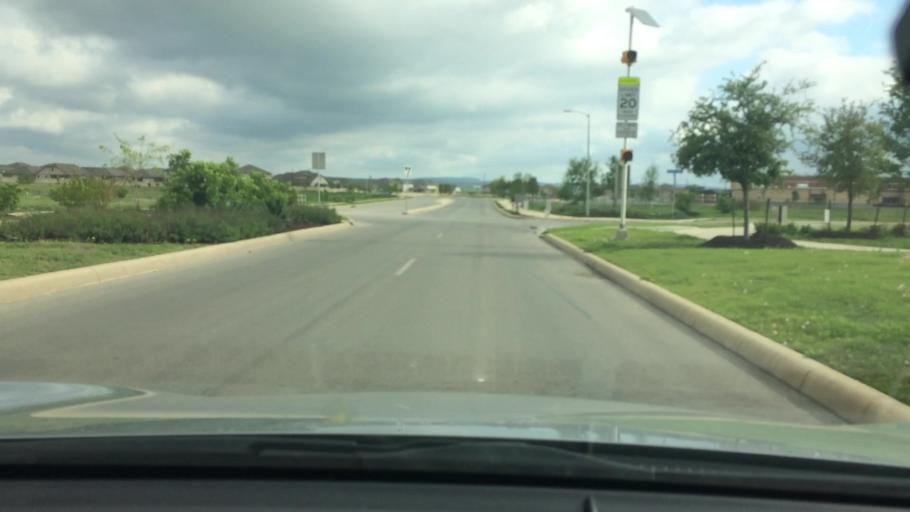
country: US
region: Texas
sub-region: Bexar County
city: Helotes
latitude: 29.5195
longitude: -98.7664
